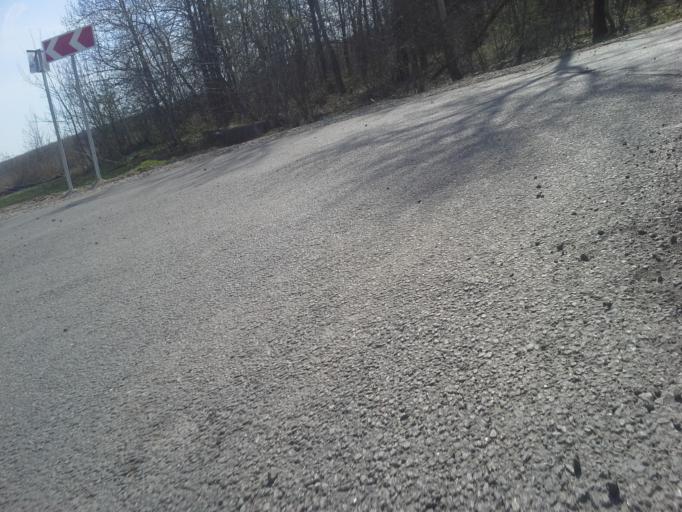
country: RU
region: Moskovskaya
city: Dubrovitsy
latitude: 55.4719
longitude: 37.4675
